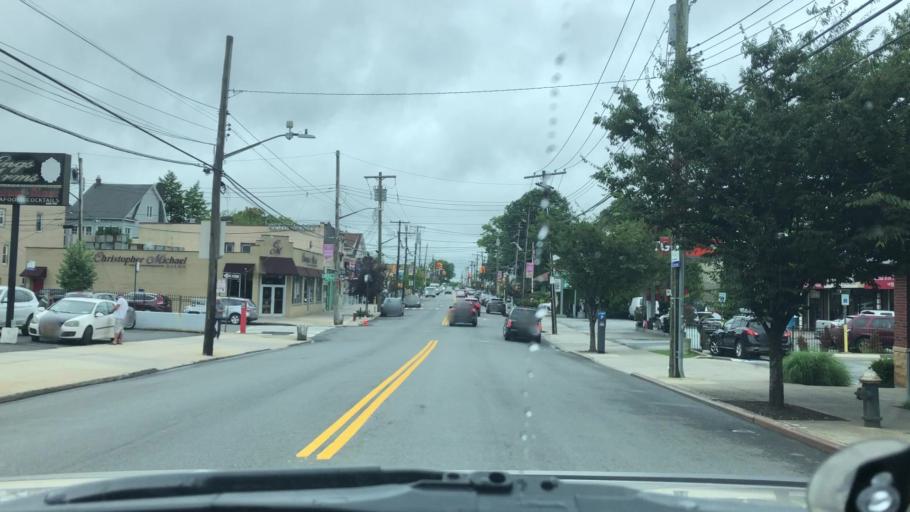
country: US
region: New Jersey
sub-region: Hudson County
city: Bayonne
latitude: 40.6305
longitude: -74.1070
